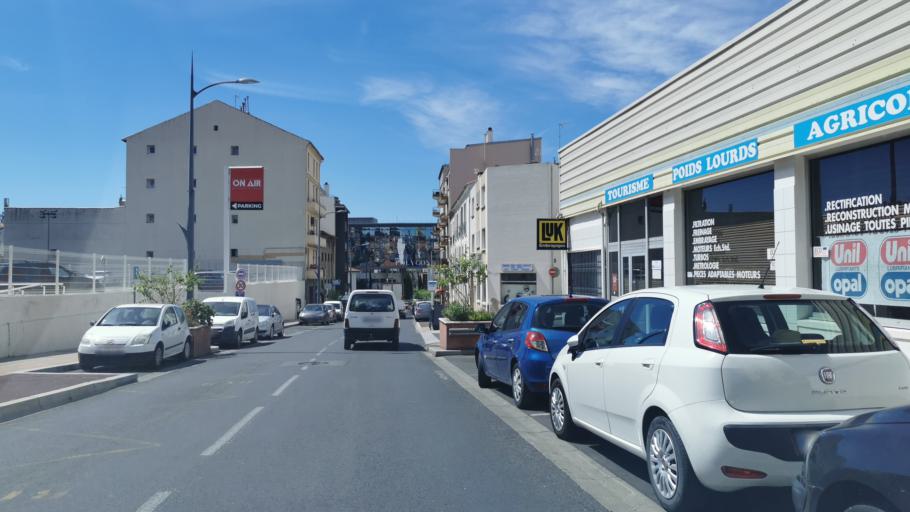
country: FR
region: Languedoc-Roussillon
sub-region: Departement de l'Herault
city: Beziers
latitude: 43.3378
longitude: 3.2253
